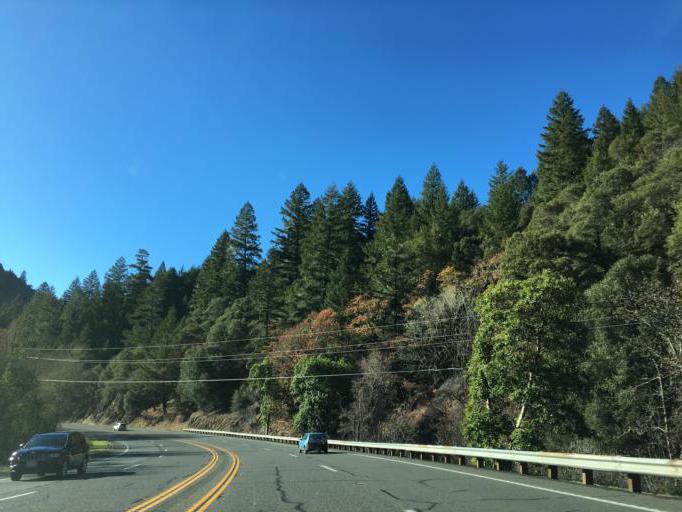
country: US
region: California
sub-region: Mendocino County
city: Brooktrails
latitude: 39.5363
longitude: -123.4068
